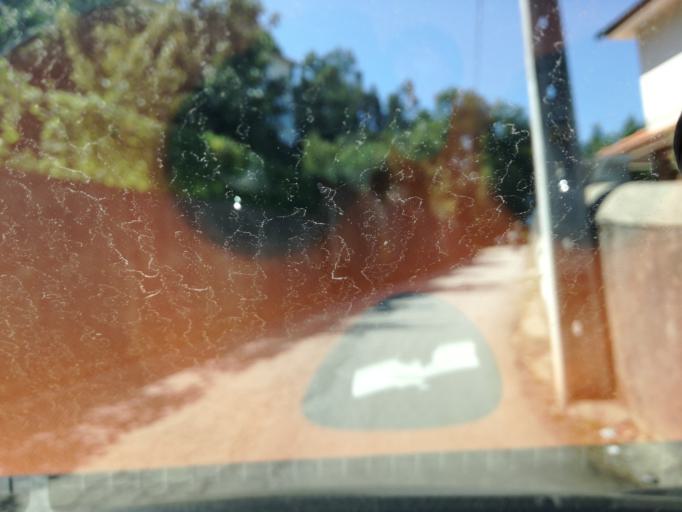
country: ES
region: Galicia
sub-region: Provincia de Pontevedra
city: O Rosal
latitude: 41.8858
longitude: -8.7878
